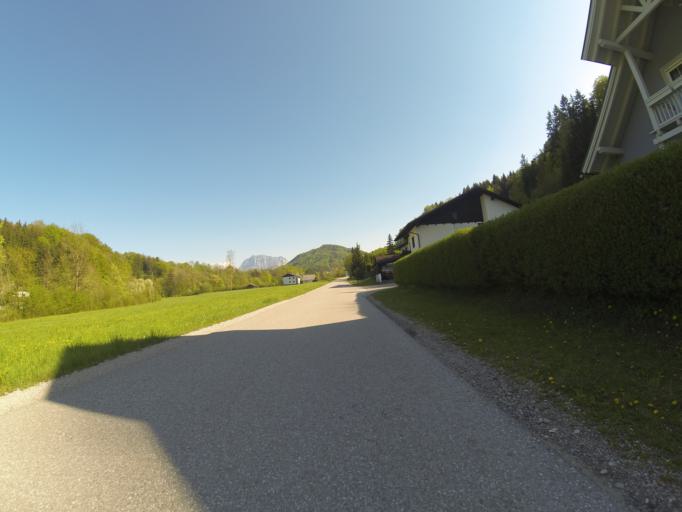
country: AT
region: Upper Austria
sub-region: Politischer Bezirk Gmunden
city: Altmunster
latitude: 47.9415
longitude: 13.7506
